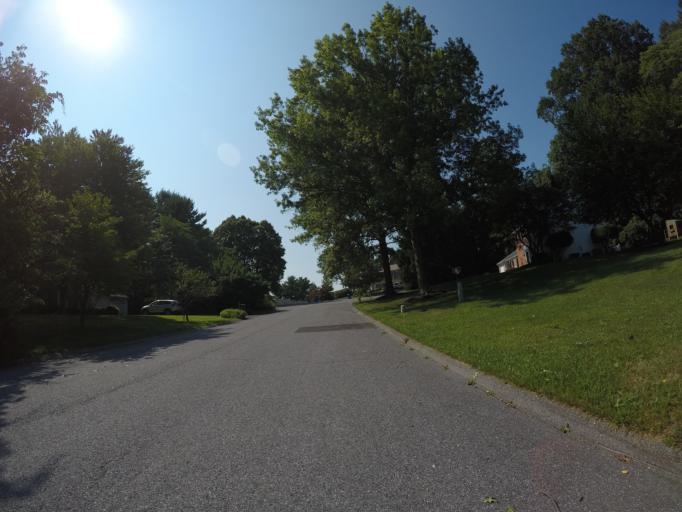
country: US
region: Maryland
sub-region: Howard County
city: Columbia
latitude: 39.2680
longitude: -76.8618
